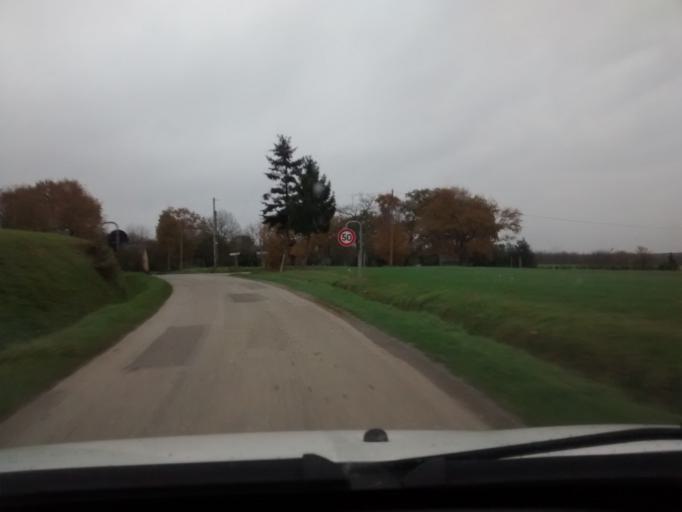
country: FR
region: Brittany
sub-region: Departement d'Ille-et-Vilaine
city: Brece
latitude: 48.1388
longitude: -1.4959
